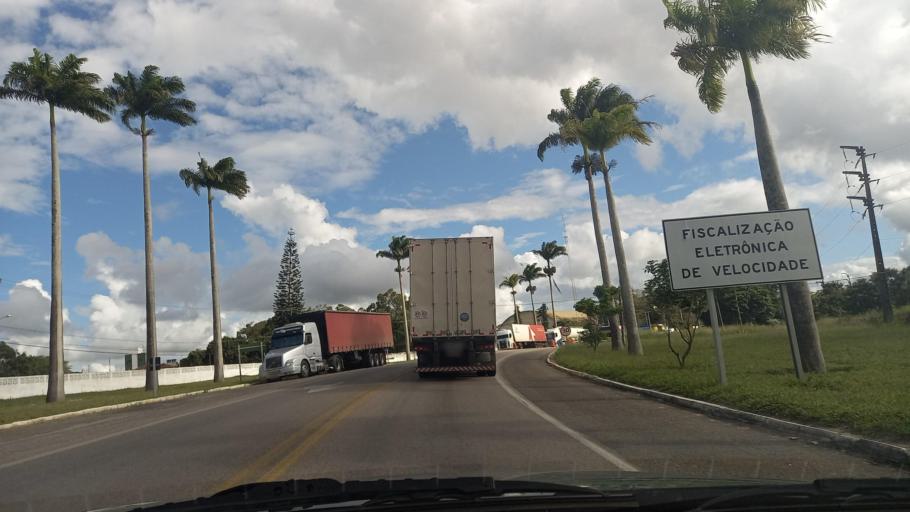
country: BR
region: Pernambuco
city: Garanhuns
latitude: -8.8682
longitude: -36.4619
